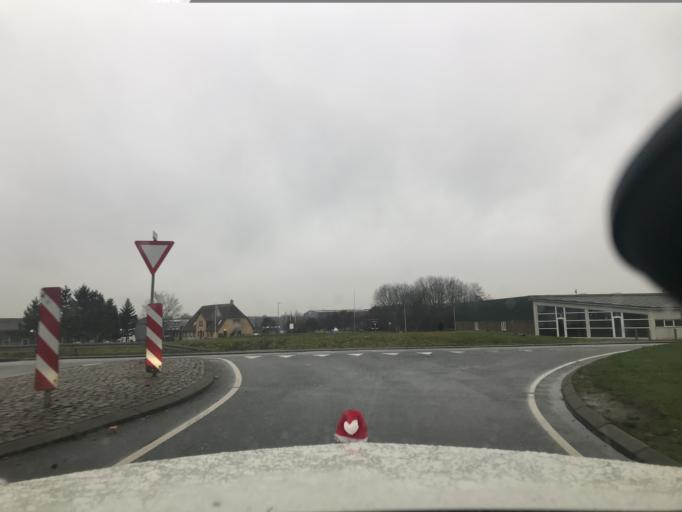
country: DK
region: South Denmark
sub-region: Aabenraa Kommune
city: Rodekro
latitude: 55.0702
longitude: 9.3559
